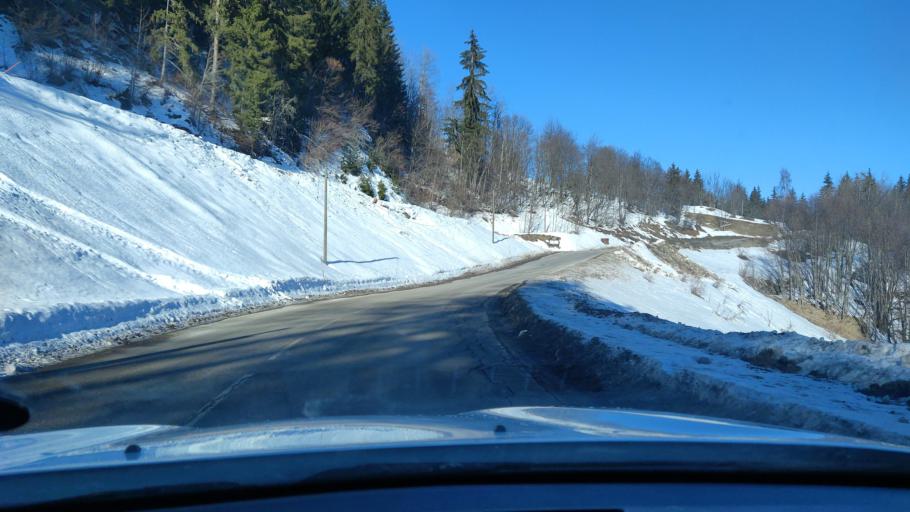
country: FR
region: Rhone-Alpes
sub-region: Departement de la Savoie
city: Meribel
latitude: 45.4329
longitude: 6.5916
